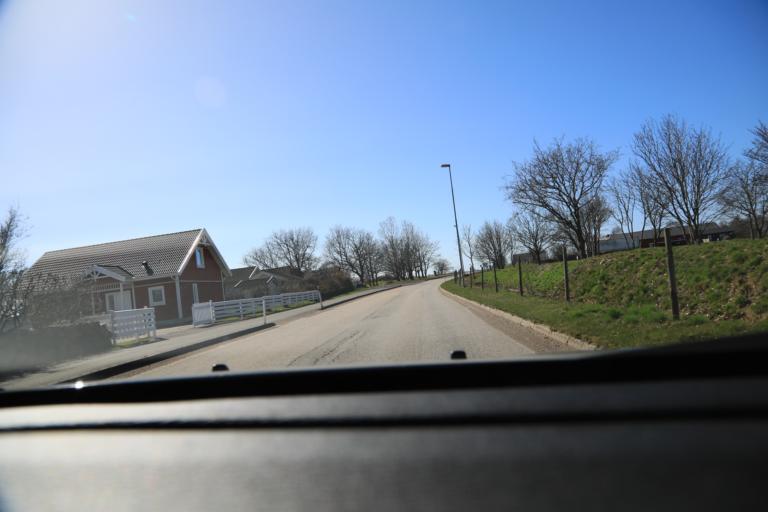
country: SE
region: Halland
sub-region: Varbergs Kommun
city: Varberg
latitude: 57.1218
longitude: 12.2246
